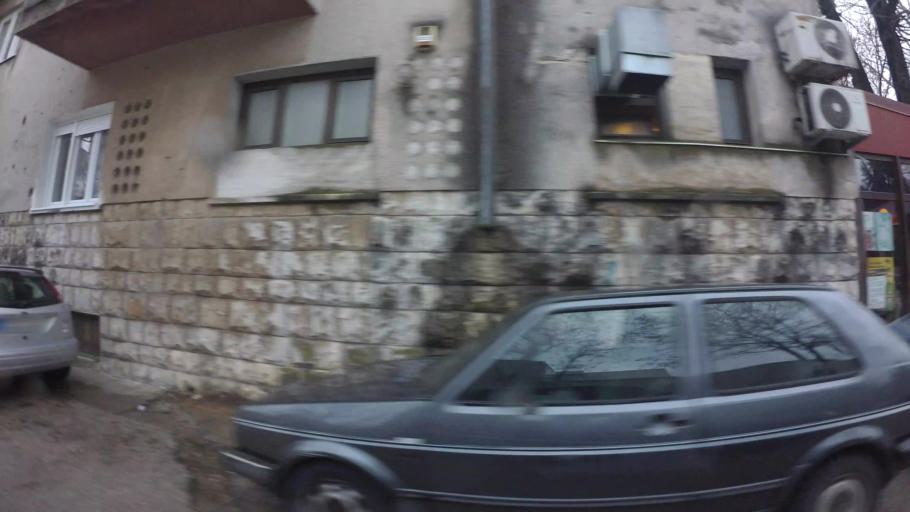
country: BA
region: Federation of Bosnia and Herzegovina
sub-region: Hercegovacko-Bosanski Kanton
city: Mostar
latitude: 43.3437
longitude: 17.7972
